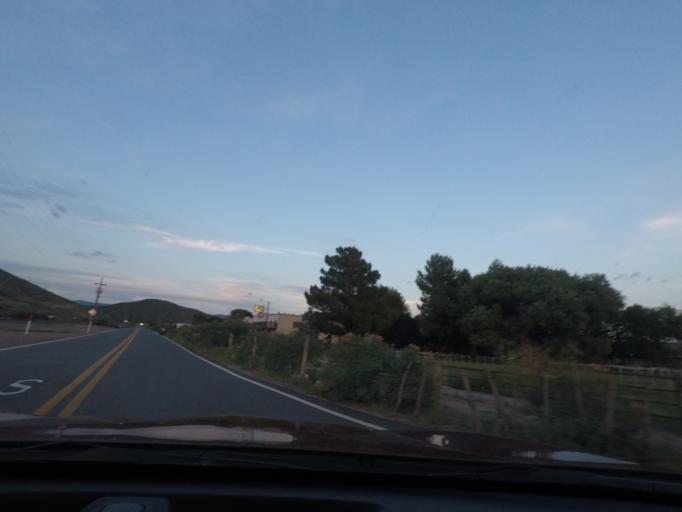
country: US
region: Arizona
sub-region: Yavapai County
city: Prescott
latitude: 34.4172
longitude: -112.7101
